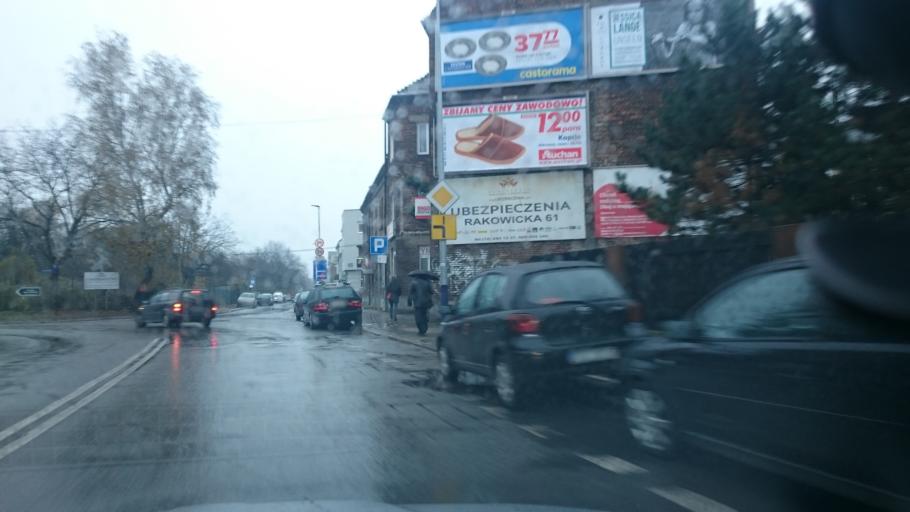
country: PL
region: Lesser Poland Voivodeship
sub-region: Krakow
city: Krakow
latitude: 50.0754
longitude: 19.9581
